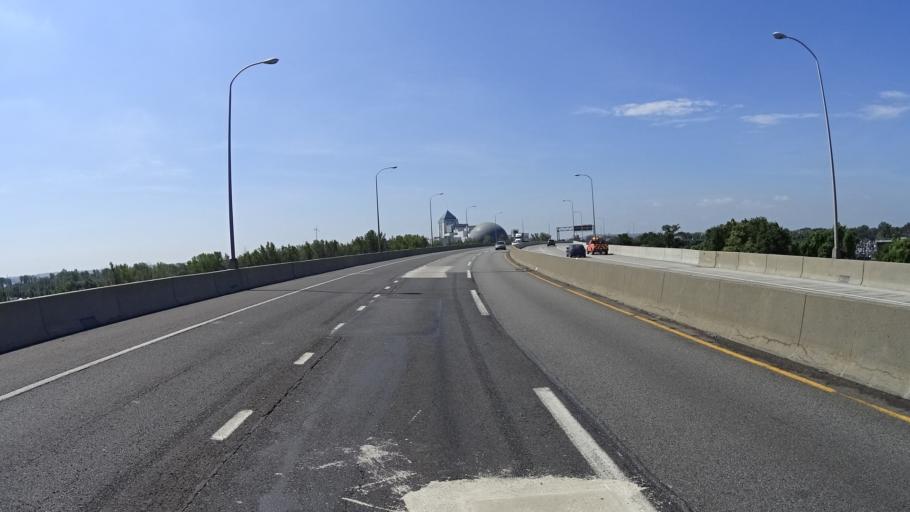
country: US
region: New Jersey
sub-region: Hudson County
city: Jersey City
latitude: 40.7125
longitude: -74.0541
